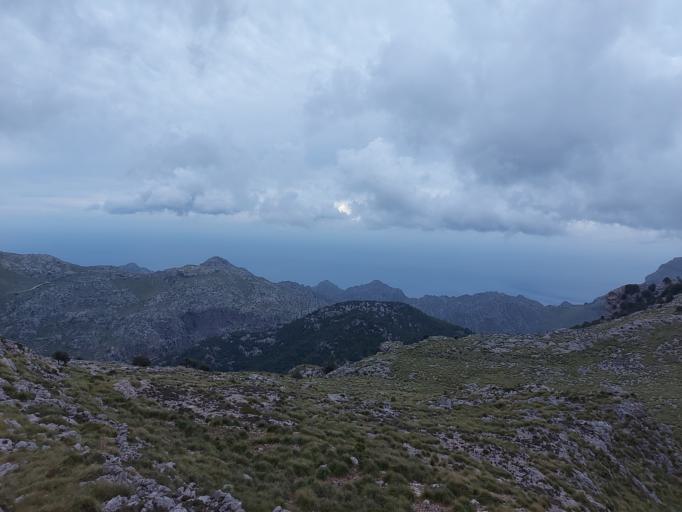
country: ES
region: Balearic Islands
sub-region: Illes Balears
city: Escorca
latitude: 39.8127
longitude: 2.8412
